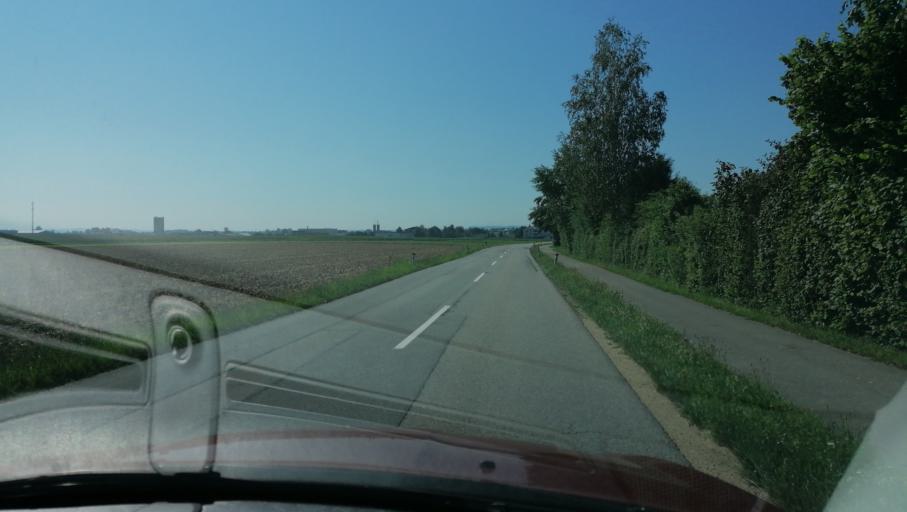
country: AT
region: Upper Austria
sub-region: Politischer Bezirk Urfahr-Umgebung
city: Feldkirchen an der Donau
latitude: 48.3532
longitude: 14.0517
